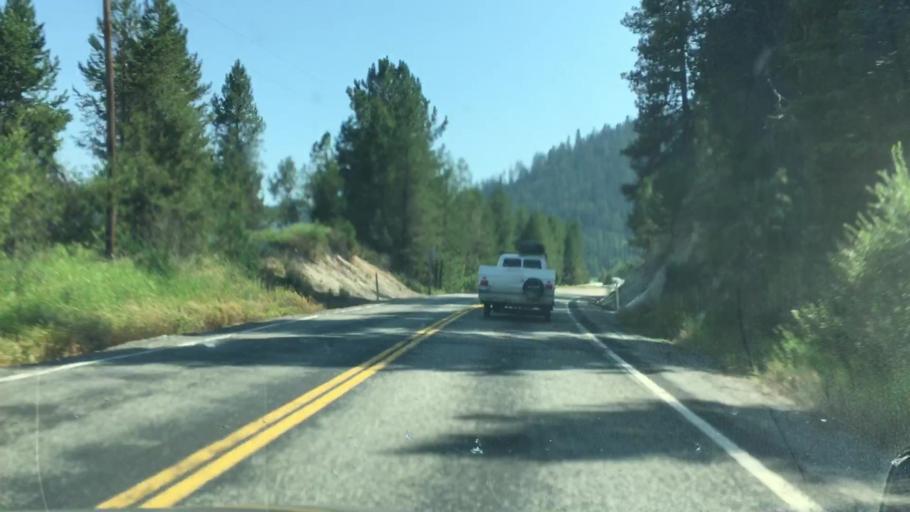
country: US
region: Idaho
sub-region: Valley County
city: Cascade
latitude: 44.3059
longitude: -116.0875
